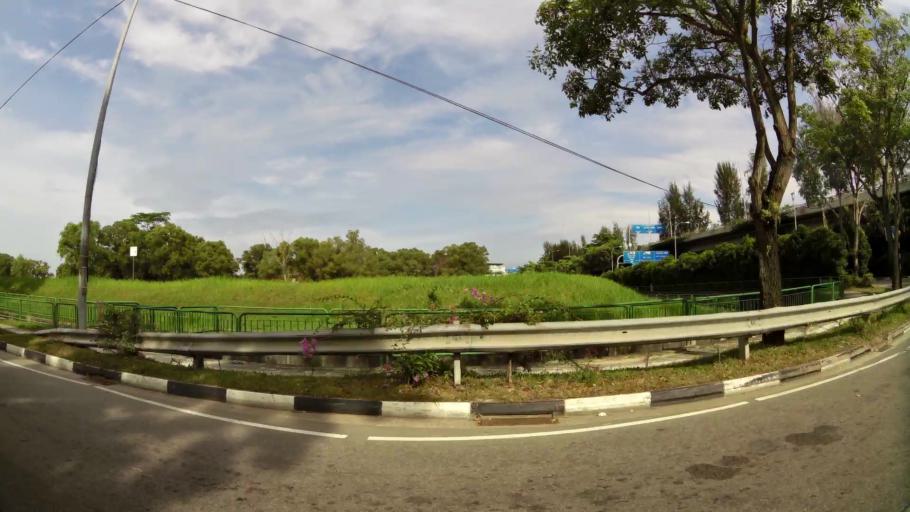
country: MY
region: Johor
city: Johor Bahru
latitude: 1.3451
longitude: 103.6389
